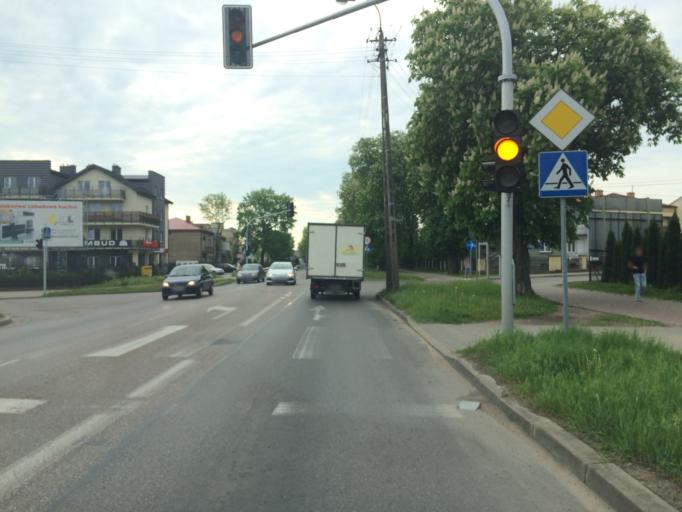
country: PL
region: Masovian Voivodeship
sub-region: Powiat mlawski
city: Mlawa
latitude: 53.1198
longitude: 20.3687
